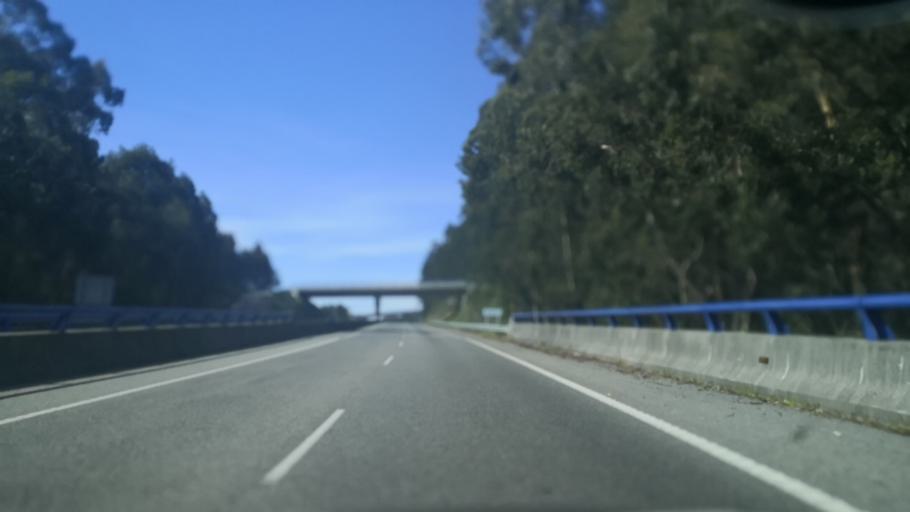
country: ES
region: Galicia
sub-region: Provincia de Pontevedra
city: Meano
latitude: 42.4585
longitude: -8.7775
